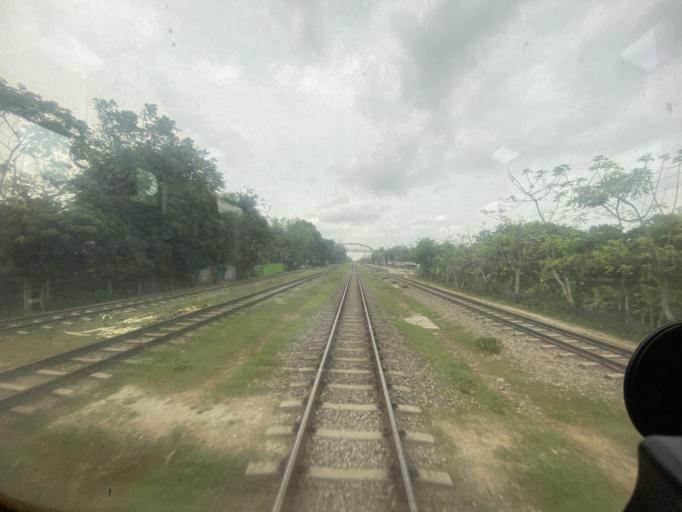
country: BD
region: Chittagong
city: Laksham
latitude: 23.2000
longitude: 91.1603
